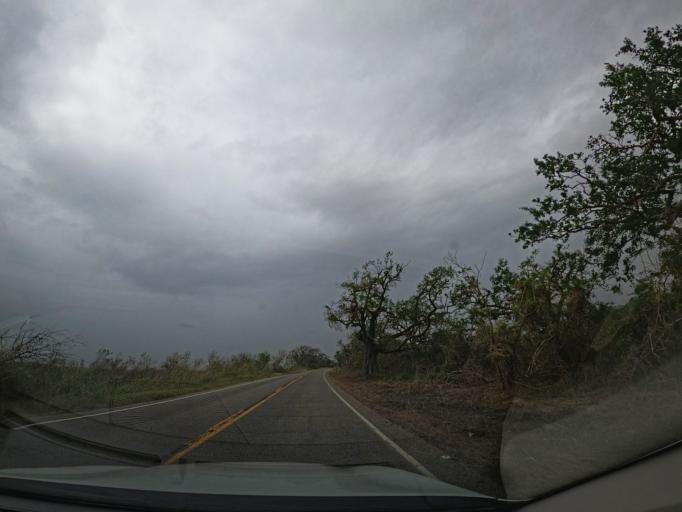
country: US
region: Louisiana
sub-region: Cameron Parish
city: Cameron
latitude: 29.7716
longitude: -93.0267
